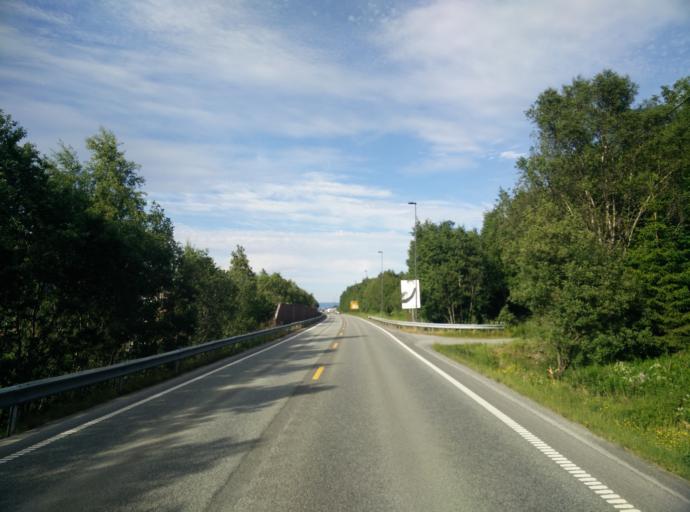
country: NO
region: Sor-Trondelag
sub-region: Orkdal
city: Orkanger
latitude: 63.3115
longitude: 9.8640
